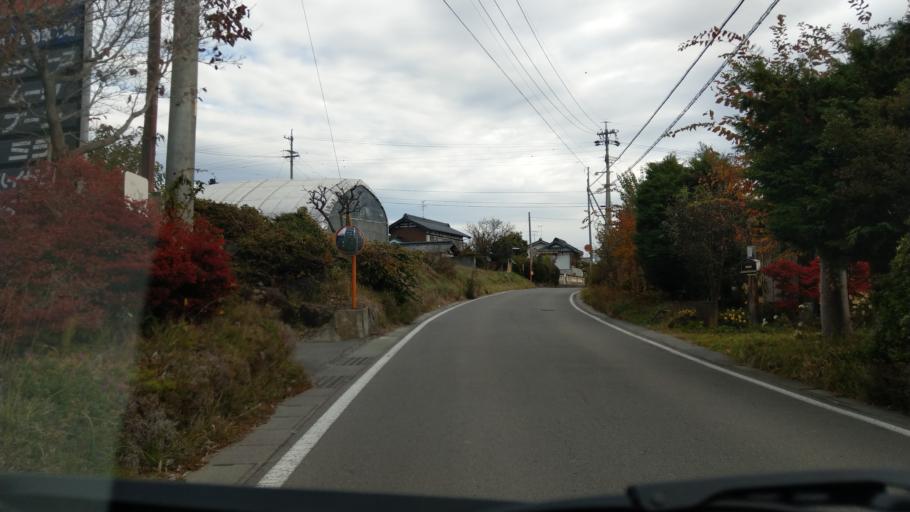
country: JP
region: Nagano
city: Komoro
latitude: 36.3221
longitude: 138.4556
